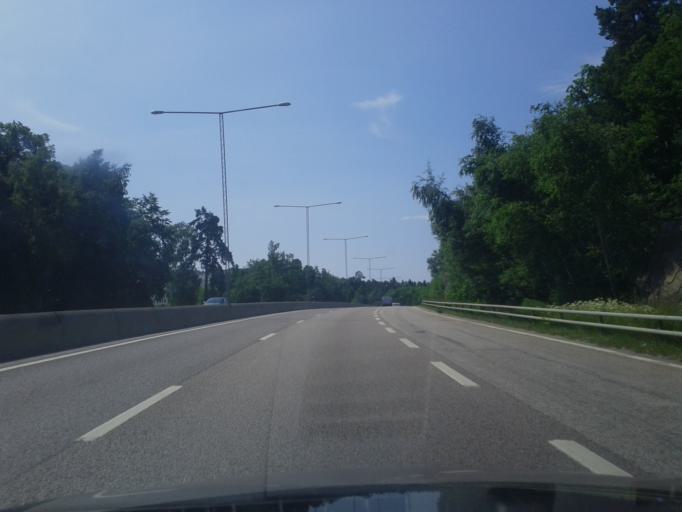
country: SE
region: Stockholm
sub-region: Huddinge Kommun
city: Huddinge
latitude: 59.2705
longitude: 18.0097
